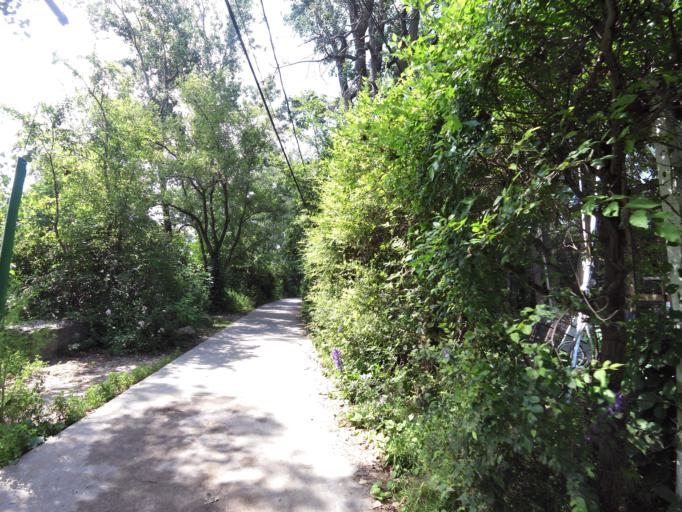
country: CA
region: Ontario
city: Toronto
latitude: 43.6299
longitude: -79.3545
